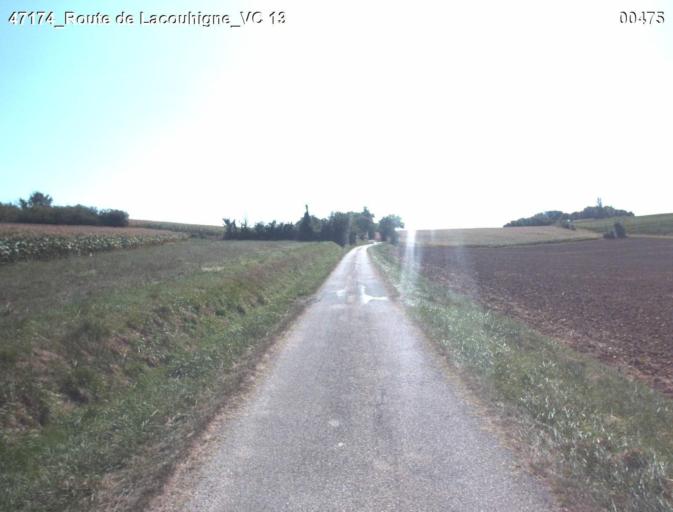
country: FR
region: Midi-Pyrenees
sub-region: Departement du Gers
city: Condom
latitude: 44.0195
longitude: 0.3869
